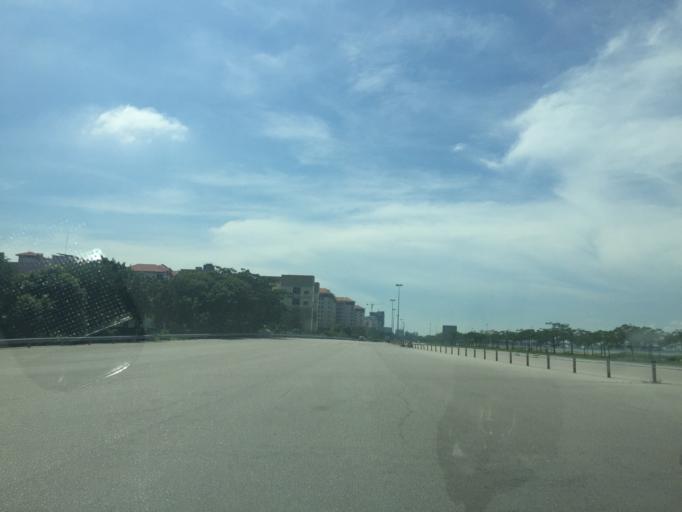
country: MY
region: Penang
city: Permatang Kuching
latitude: 5.4302
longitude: 100.3766
